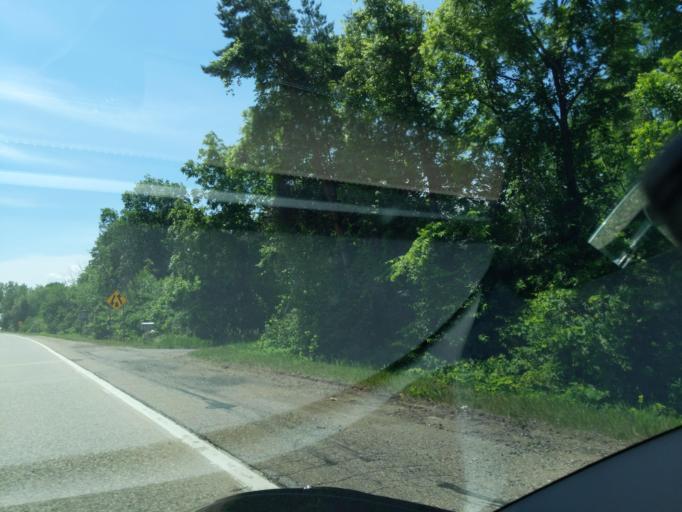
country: US
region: Michigan
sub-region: Kent County
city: Forest Hills
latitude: 42.9514
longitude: -85.4647
